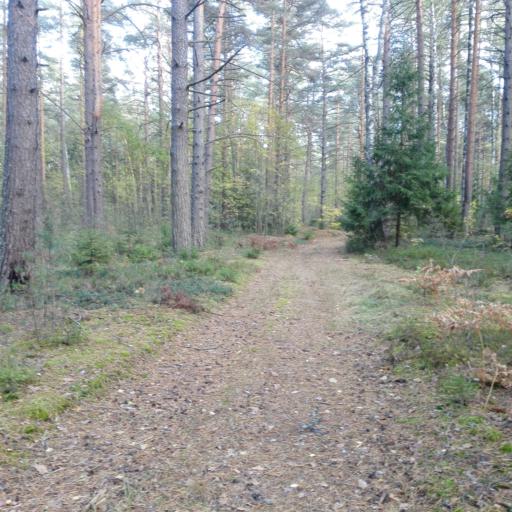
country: RU
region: Vladimir
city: Kommunar
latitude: 56.0762
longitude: 40.5135
